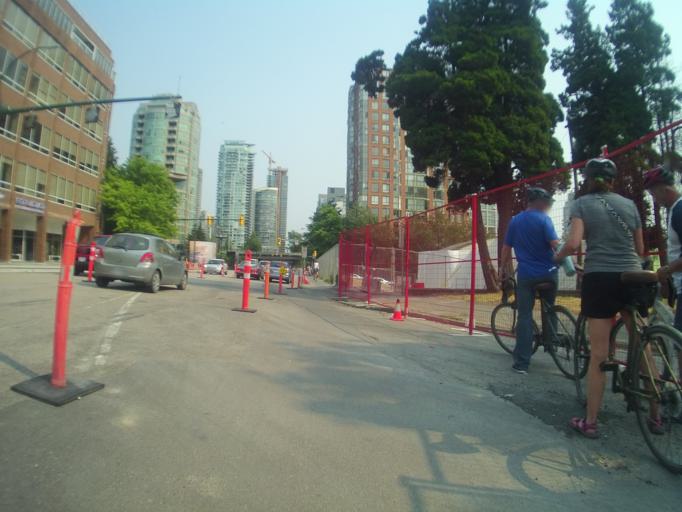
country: CA
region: British Columbia
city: West End
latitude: 49.2765
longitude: -123.1323
